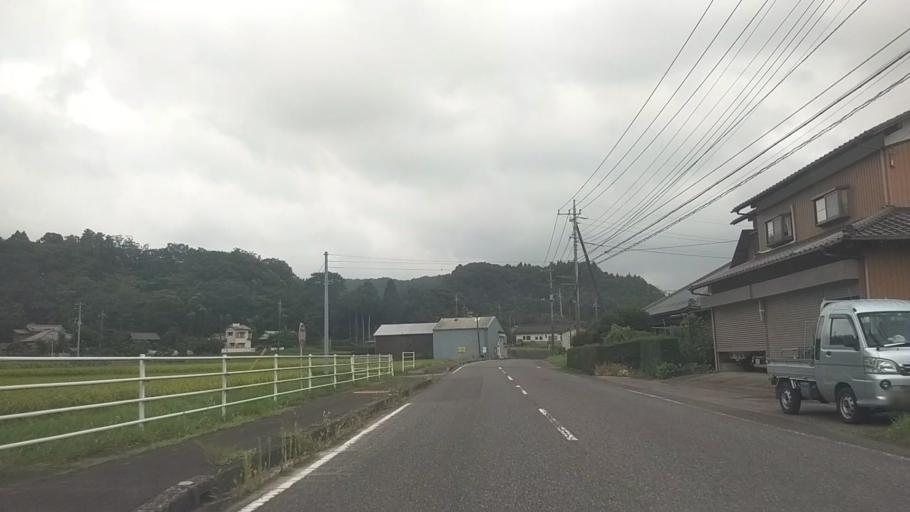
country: JP
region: Chiba
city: Kawaguchi
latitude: 35.2450
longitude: 140.0813
